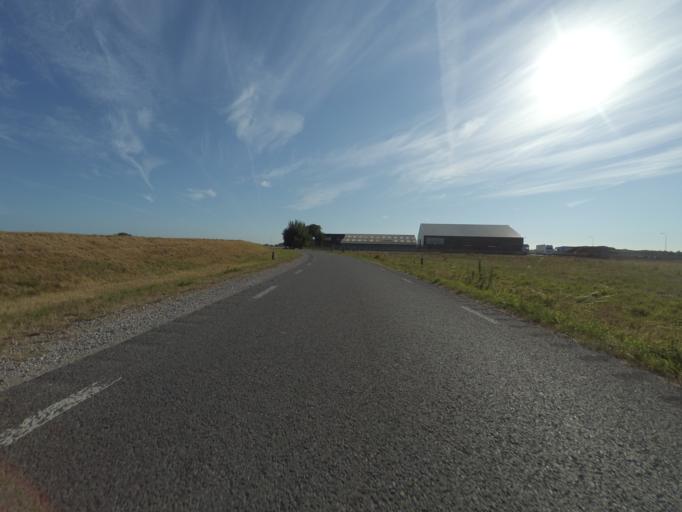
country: NL
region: Gelderland
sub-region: Gemeente Elburg
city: Elburg
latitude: 52.4359
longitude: 5.8147
